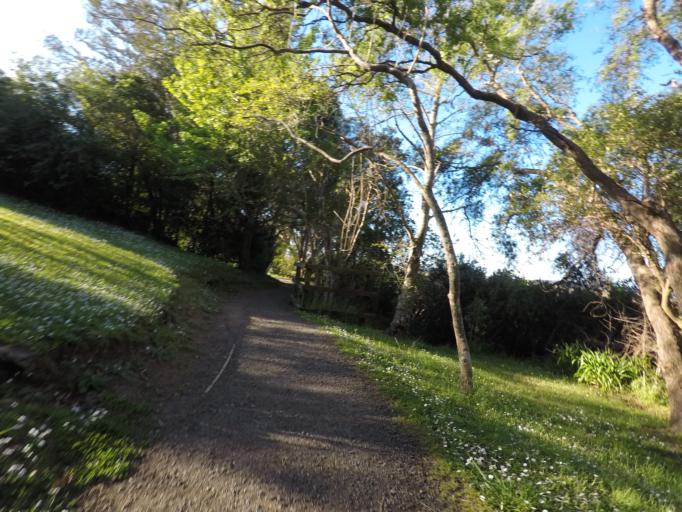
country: NZ
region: Auckland
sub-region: Auckland
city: Rosebank
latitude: -36.8270
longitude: 174.6516
